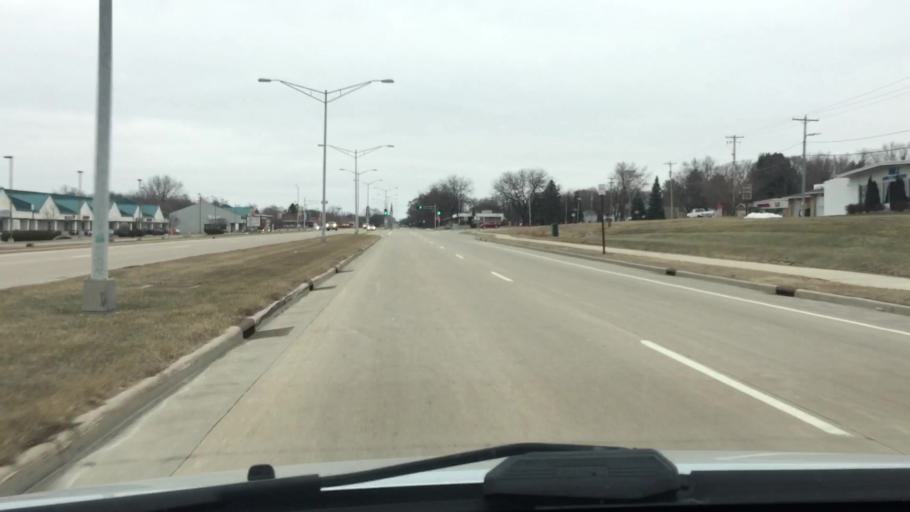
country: US
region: Wisconsin
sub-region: Jefferson County
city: Watertown
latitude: 43.1728
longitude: -88.7321
